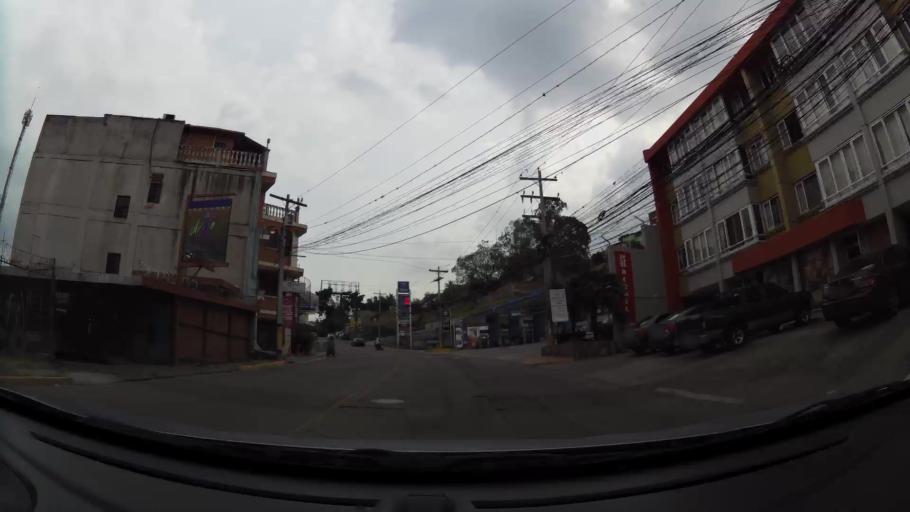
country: HN
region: Francisco Morazan
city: Tegucigalpa
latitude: 14.0905
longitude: -87.1906
